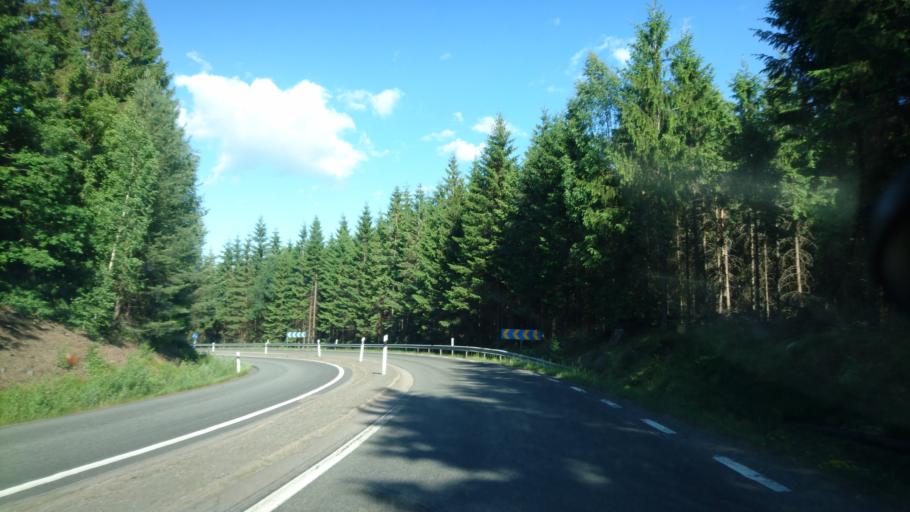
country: SE
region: Skane
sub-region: Osby Kommun
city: Lonsboda
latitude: 56.3879
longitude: 14.3708
